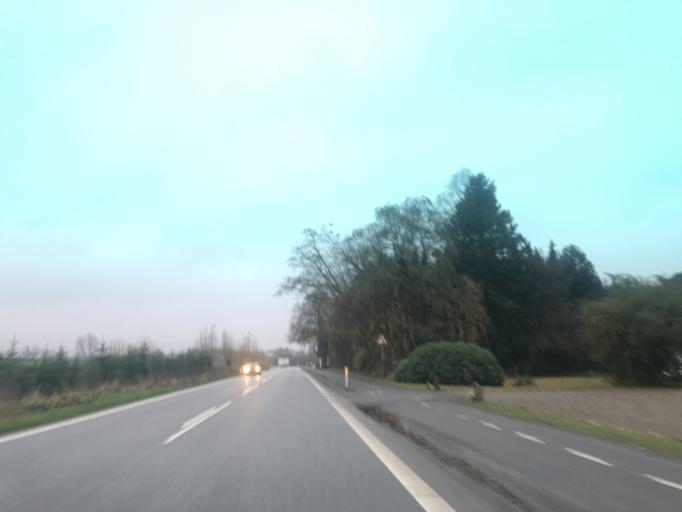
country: DK
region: South Denmark
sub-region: Nyborg Kommune
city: Ullerslev
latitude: 55.2729
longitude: 10.6792
